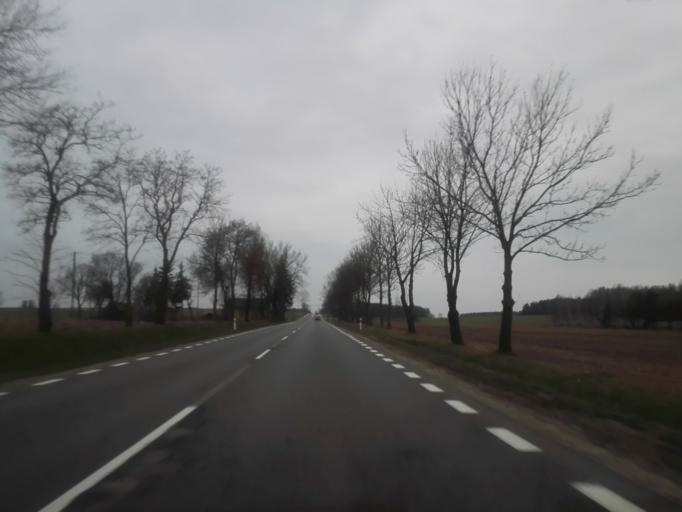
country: PL
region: Podlasie
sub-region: Powiat kolnenski
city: Stawiski
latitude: 53.4555
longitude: 22.1913
